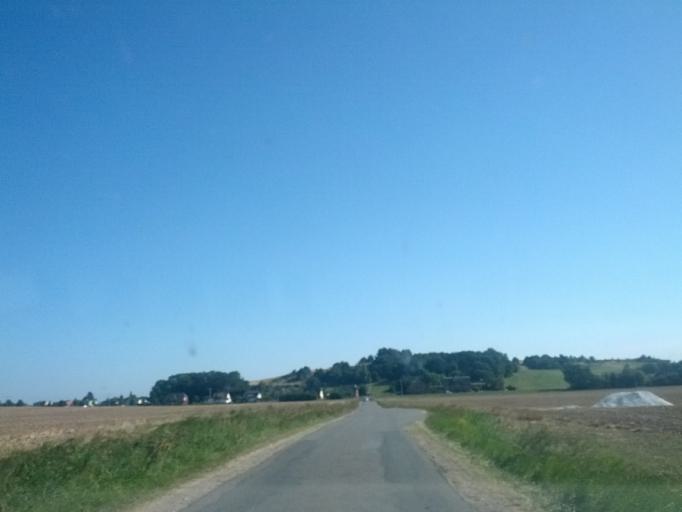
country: DE
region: Mecklenburg-Vorpommern
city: Ostseebad Sellin
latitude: 54.3345
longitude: 13.6872
